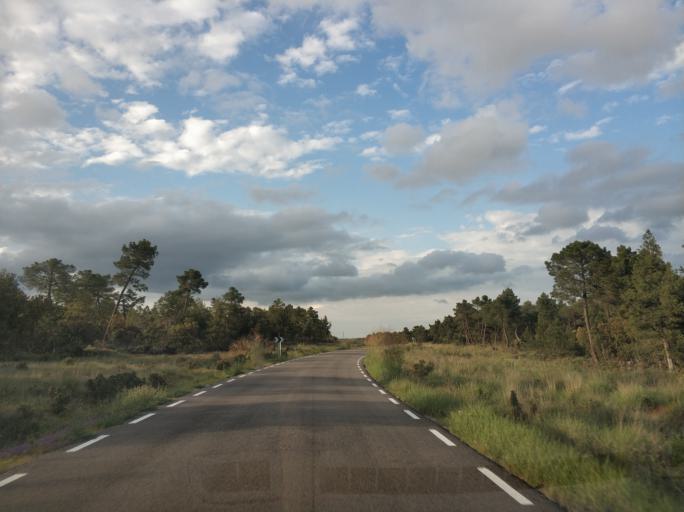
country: ES
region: Castille and Leon
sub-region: Provincia de Burgos
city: San Juan del Monte
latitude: 41.6627
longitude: -3.5316
